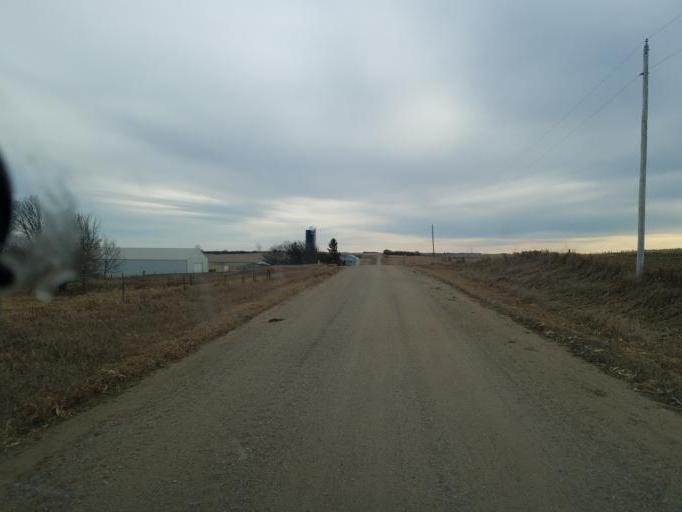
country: US
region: Nebraska
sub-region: Knox County
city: Bloomfield
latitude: 42.5250
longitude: -97.7508
